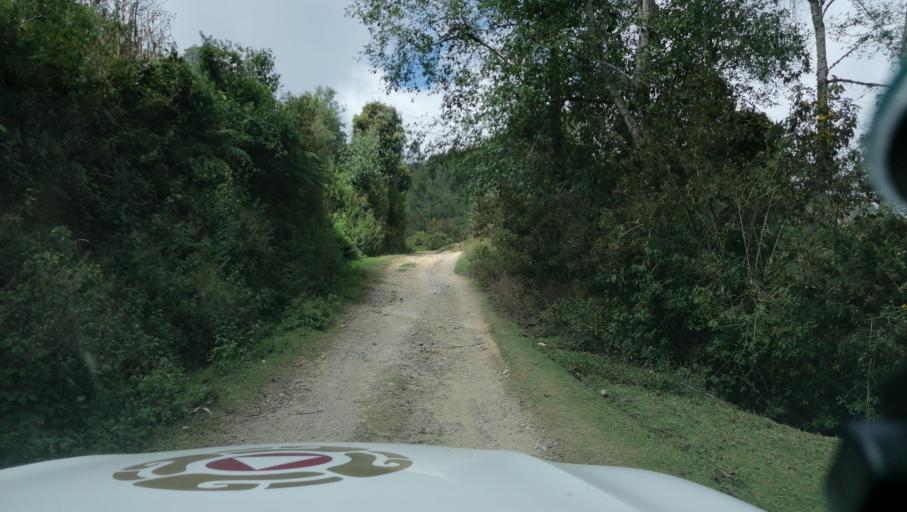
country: MX
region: Chiapas
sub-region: Cacahoatan
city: Benito Juarez
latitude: 15.1998
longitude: -92.2218
